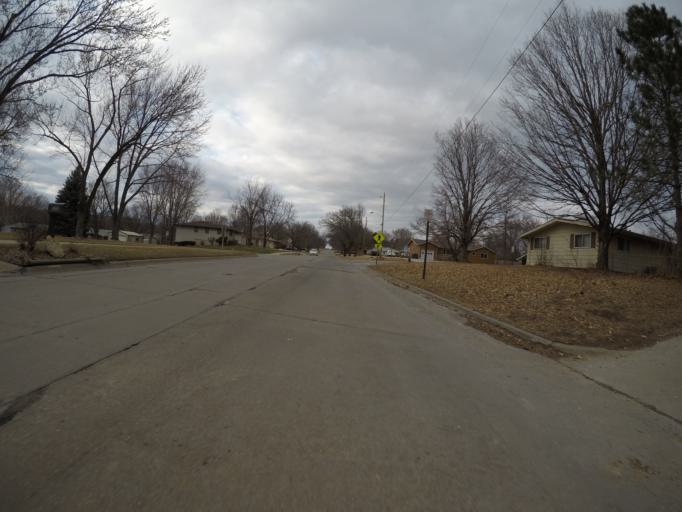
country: US
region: Kansas
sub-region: Riley County
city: Manhattan
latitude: 39.1923
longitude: -96.6168
